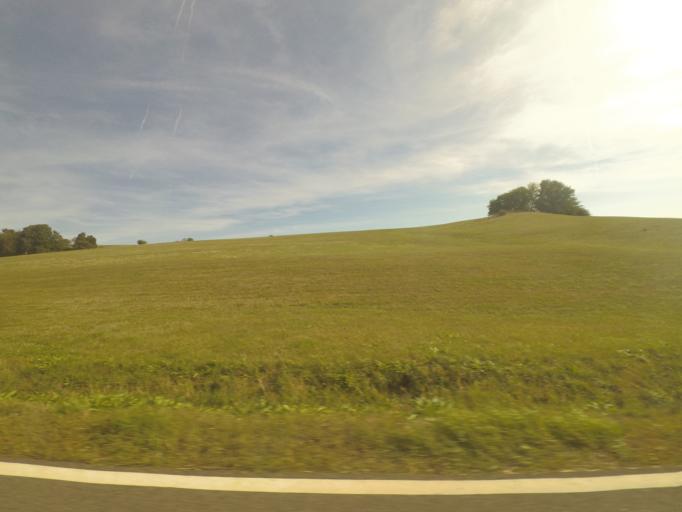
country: DE
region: Thuringia
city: Oberkatz
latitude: 50.5733
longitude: 10.2431
